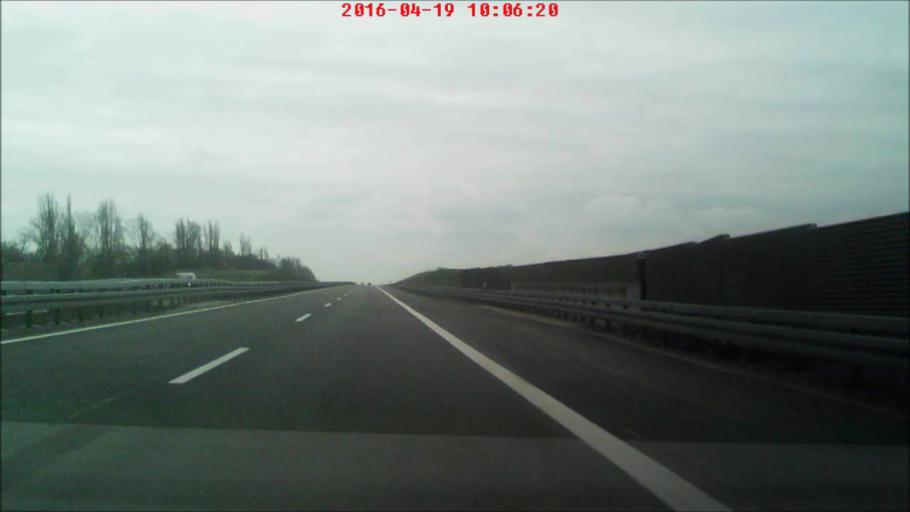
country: DE
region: Thuringia
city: Schillingstedt
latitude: 51.2112
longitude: 11.1851
